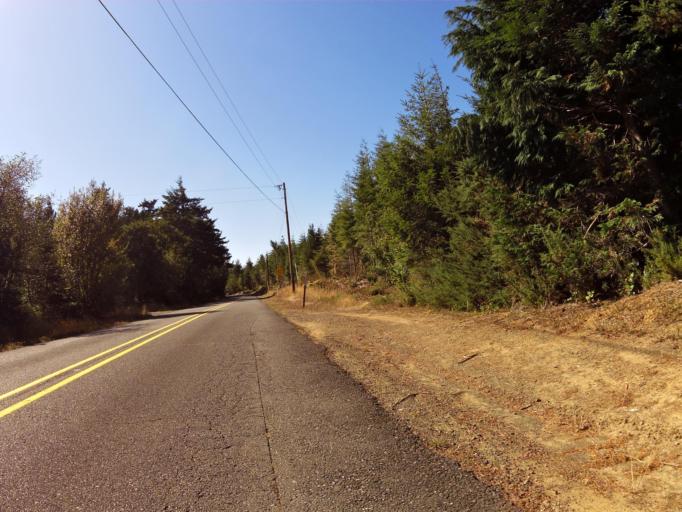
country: US
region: Oregon
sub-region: Coos County
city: Bandon
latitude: 43.2142
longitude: -124.3654
